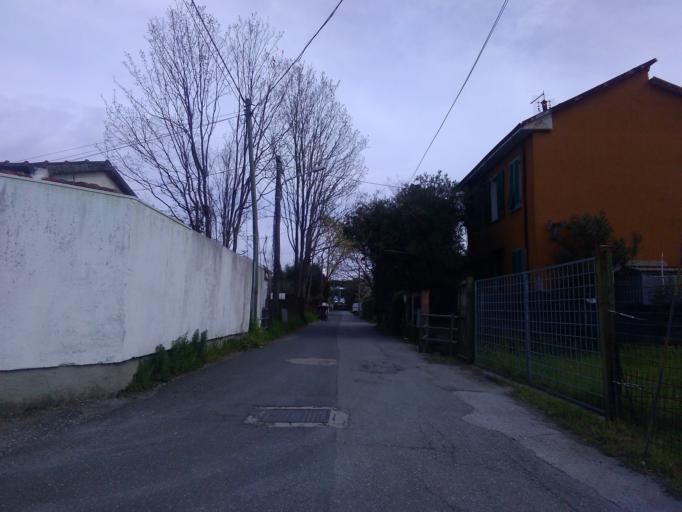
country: IT
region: Tuscany
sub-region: Provincia di Massa-Carrara
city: Marina di Carrara
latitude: 44.0536
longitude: 10.0372
